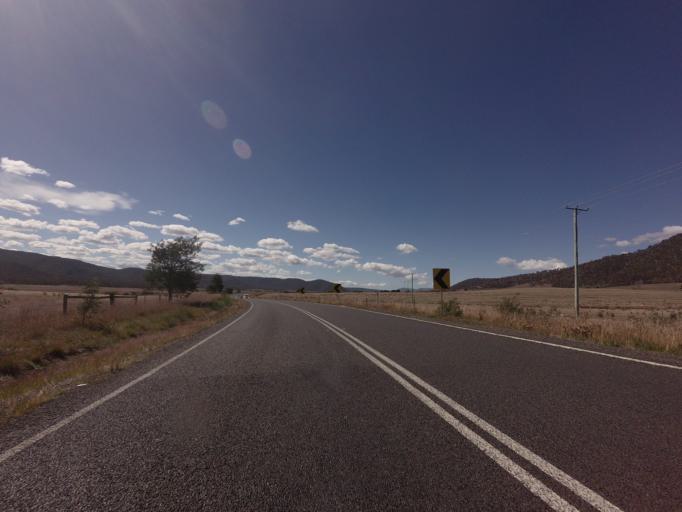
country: AU
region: Tasmania
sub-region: Break O'Day
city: St Helens
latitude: -41.7060
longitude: 147.8489
